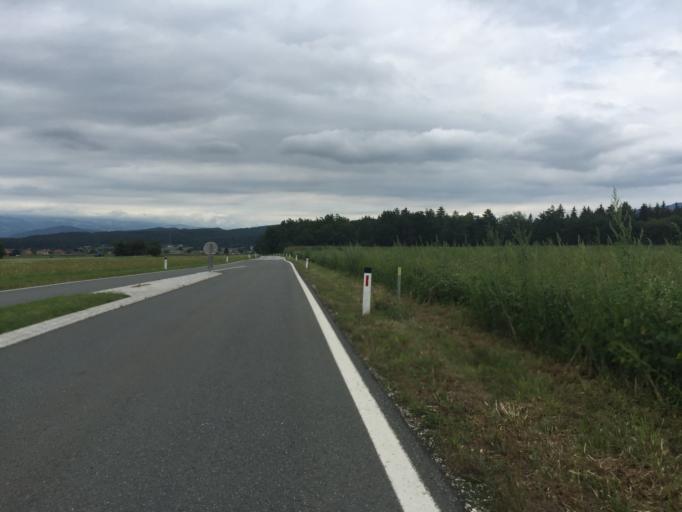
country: AT
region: Carinthia
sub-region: Politischer Bezirk Volkermarkt
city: Feistritz ob Bleiburg
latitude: 46.5595
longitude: 14.7671
